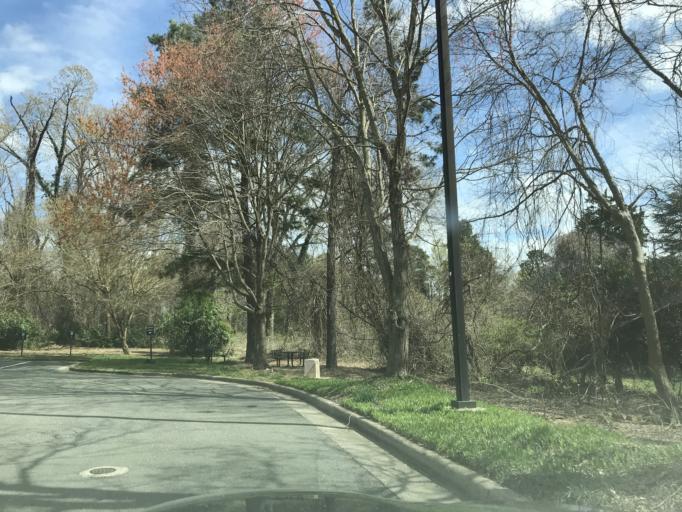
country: US
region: North Carolina
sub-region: Orange County
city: Chapel Hill
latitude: 35.8998
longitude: -79.0560
